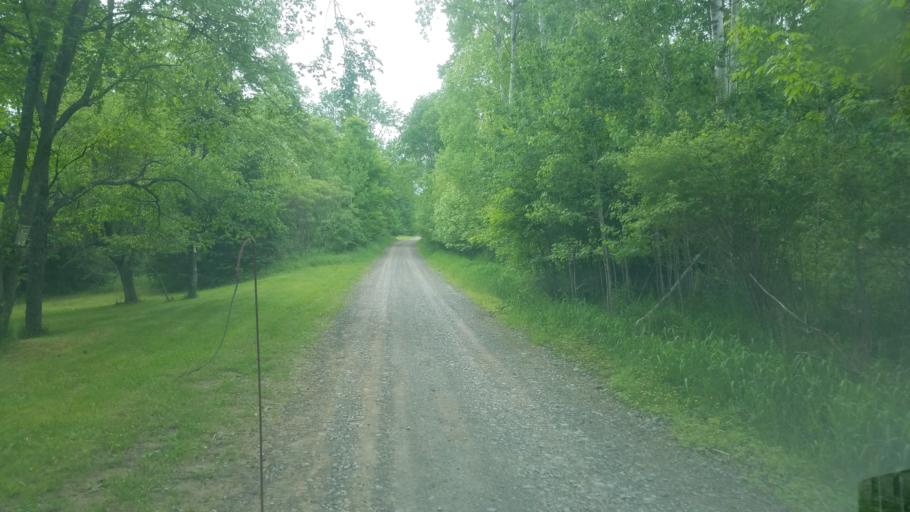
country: US
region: Pennsylvania
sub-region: Tioga County
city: Westfield
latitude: 41.9276
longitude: -77.6912
